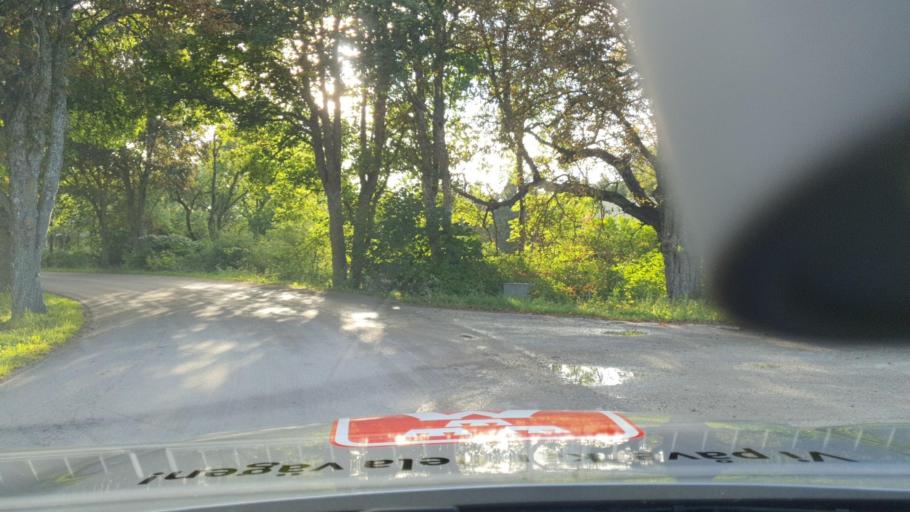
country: SE
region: Gotland
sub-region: Gotland
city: Hemse
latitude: 57.4030
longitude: 18.5287
